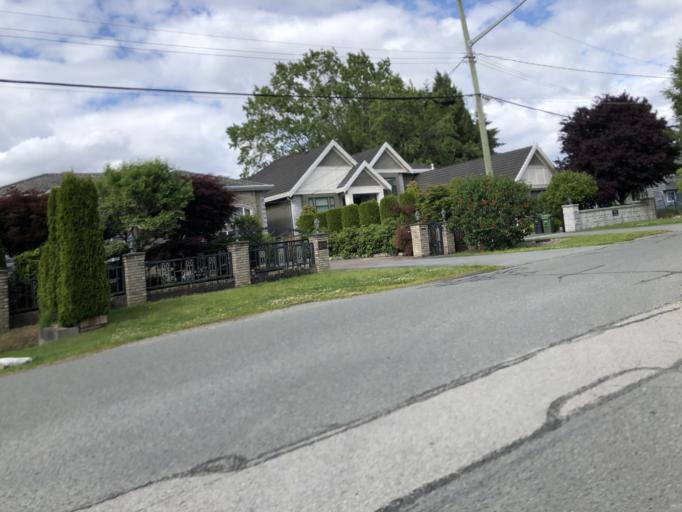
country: CA
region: British Columbia
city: Richmond
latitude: 49.1546
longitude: -123.1338
